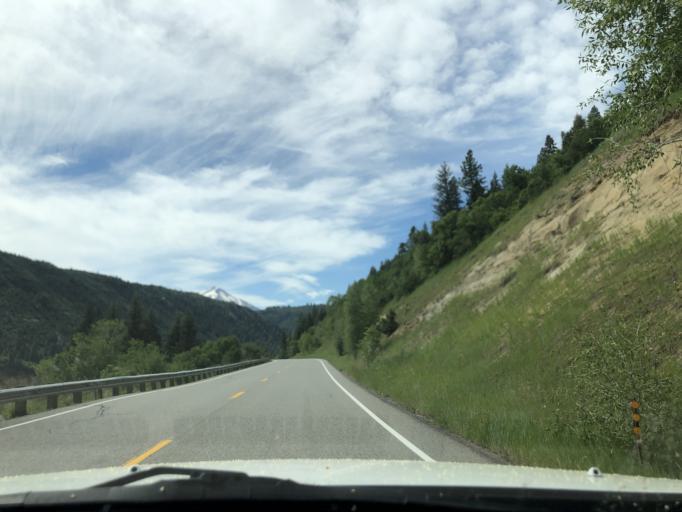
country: US
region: Colorado
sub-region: Delta County
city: Paonia
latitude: 38.9754
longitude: -107.3425
